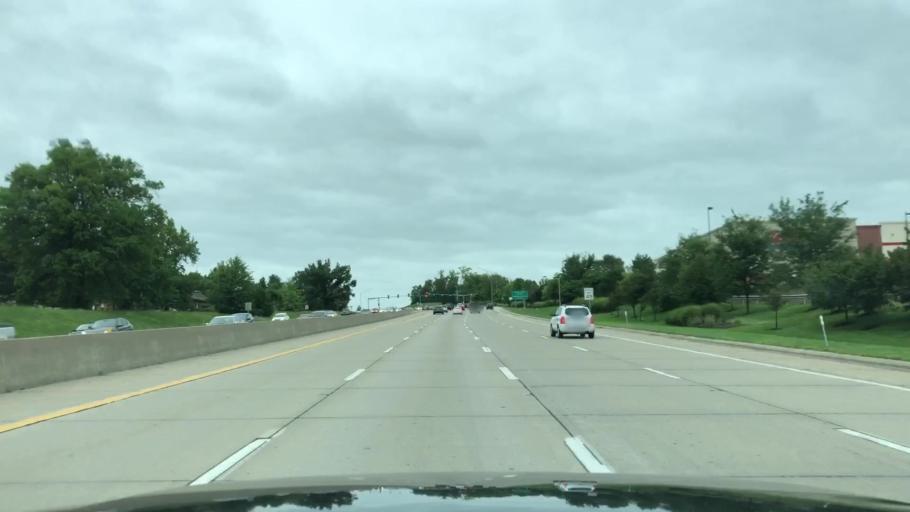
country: US
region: Missouri
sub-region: Saint Louis County
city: Manchester
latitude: 38.5960
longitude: -90.5086
